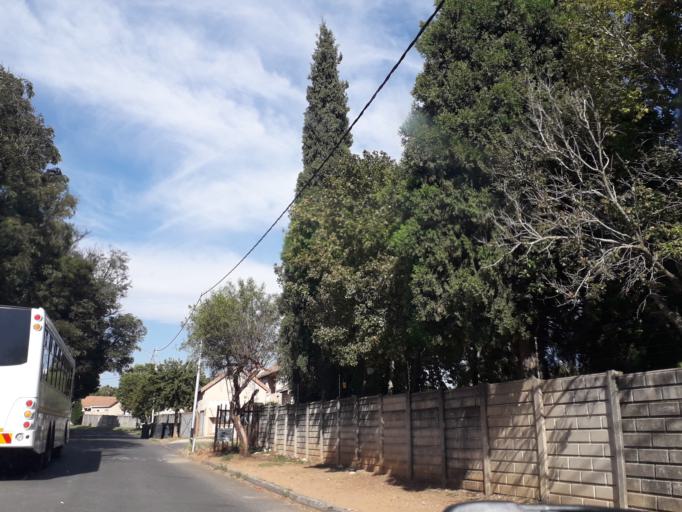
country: ZA
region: Gauteng
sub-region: City of Johannesburg Metropolitan Municipality
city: Modderfontein
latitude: -26.1270
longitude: 28.1015
